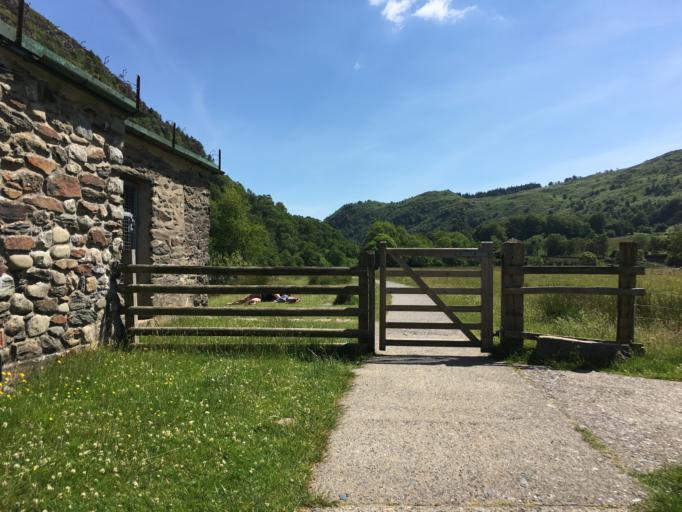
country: GB
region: Wales
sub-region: Gwynedd
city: Penrhyndeudraeth
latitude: 53.0088
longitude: -4.1006
